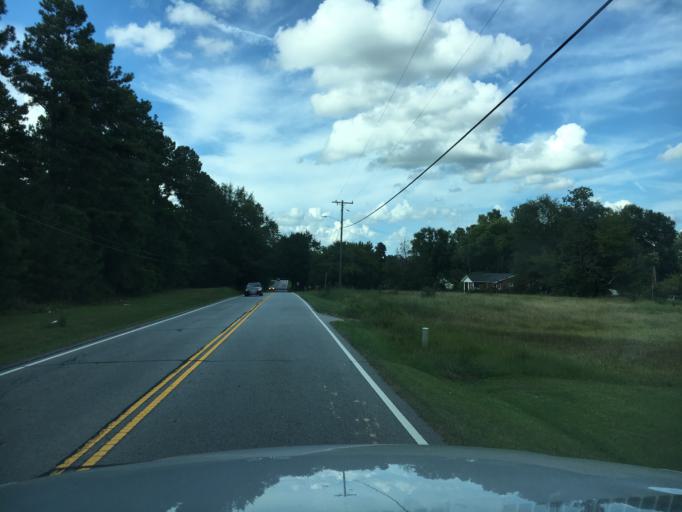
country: US
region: South Carolina
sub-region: Greenville County
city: Fountain Inn
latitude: 34.7017
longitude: -82.1811
